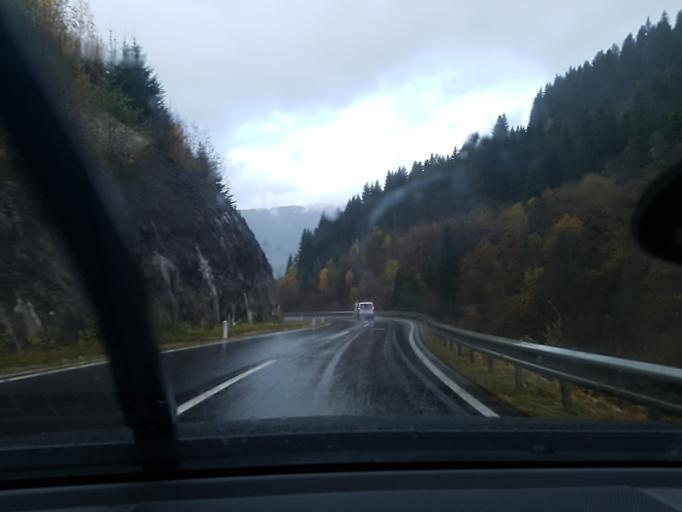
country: AT
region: Styria
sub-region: Politischer Bezirk Liezen
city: Trieben
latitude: 47.4742
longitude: 14.4848
